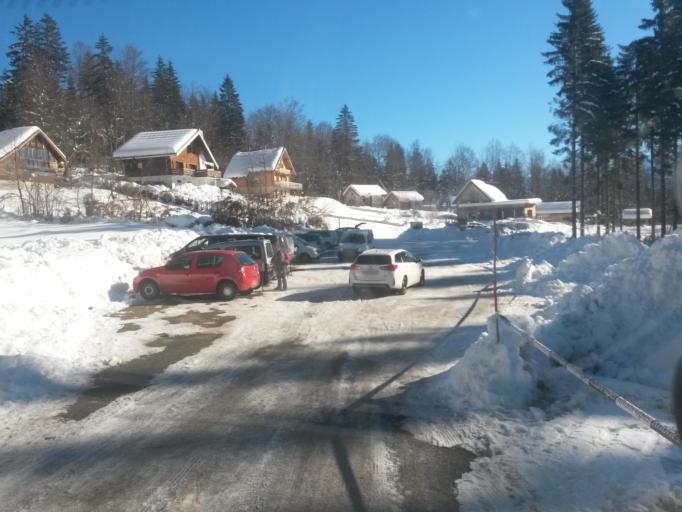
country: FR
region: Rhone-Alpes
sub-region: Departement de l'Isere
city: Le Touvet
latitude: 45.3549
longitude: 5.9186
